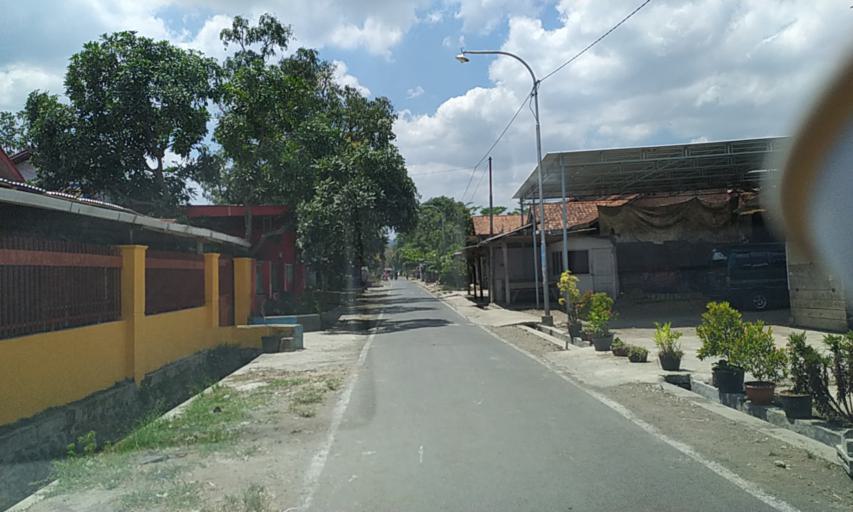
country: ID
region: Central Java
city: Sampang
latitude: -7.5651
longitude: 109.1979
